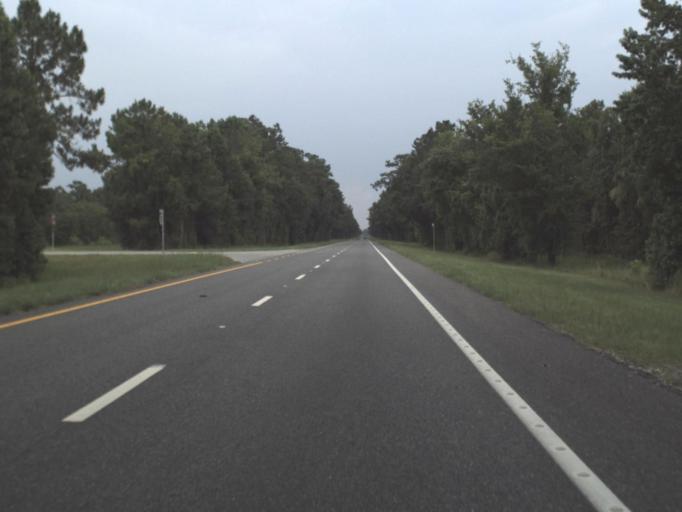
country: US
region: Florida
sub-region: Levy County
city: Bronson
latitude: 29.2742
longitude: -82.7364
